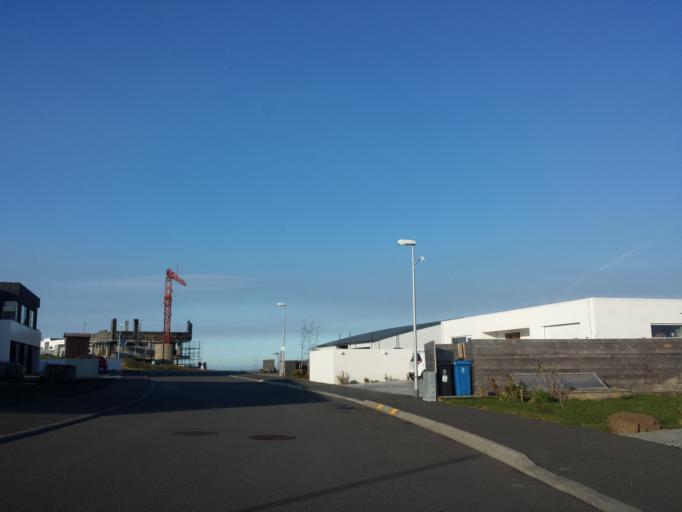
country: IS
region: Capital Region
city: Reykjavik
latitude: 64.0856
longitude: -21.8364
